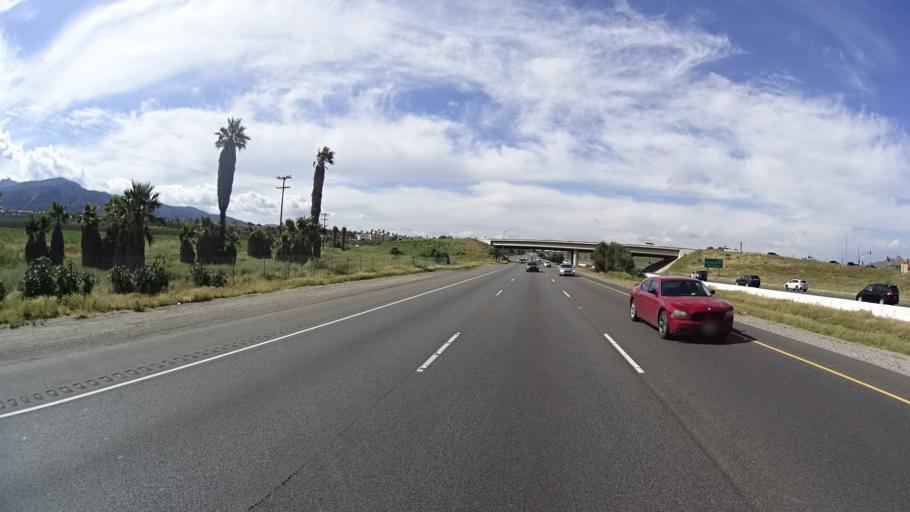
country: US
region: California
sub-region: Riverside County
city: El Cerrito
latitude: 33.8200
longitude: -117.5171
